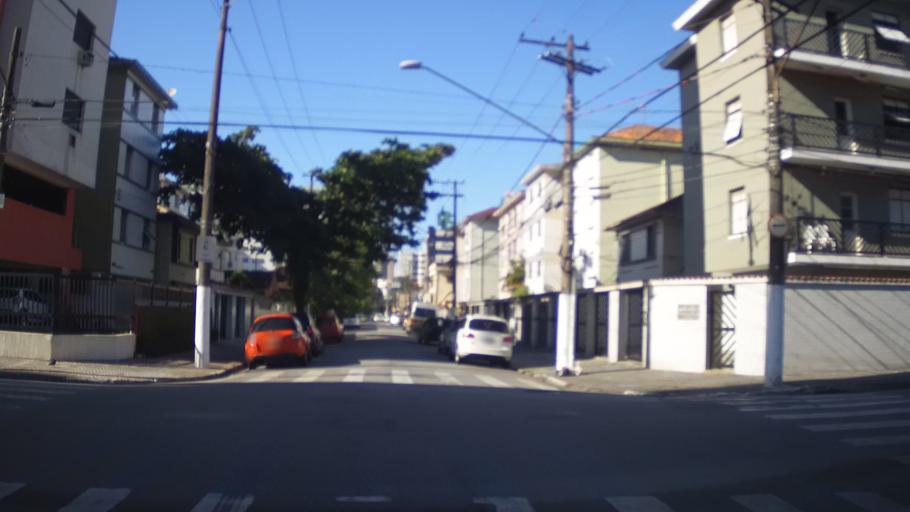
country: BR
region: Sao Paulo
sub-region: Santos
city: Santos
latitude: -23.9573
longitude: -46.3470
